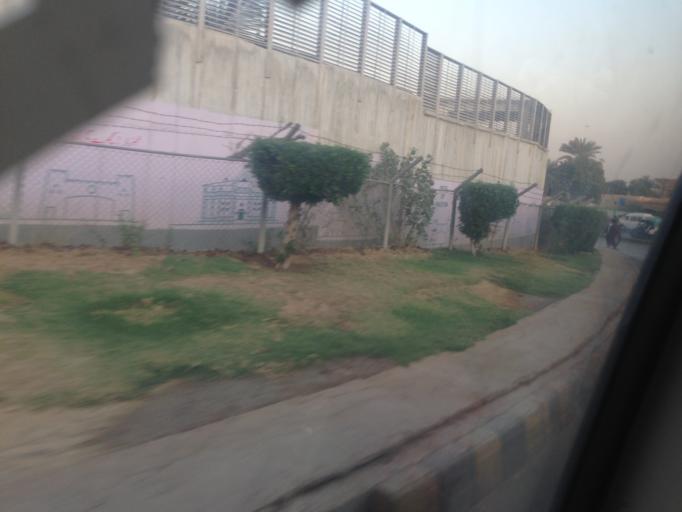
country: PK
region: Sindh
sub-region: Karachi District
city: Karachi
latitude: 24.8755
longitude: 67.0962
